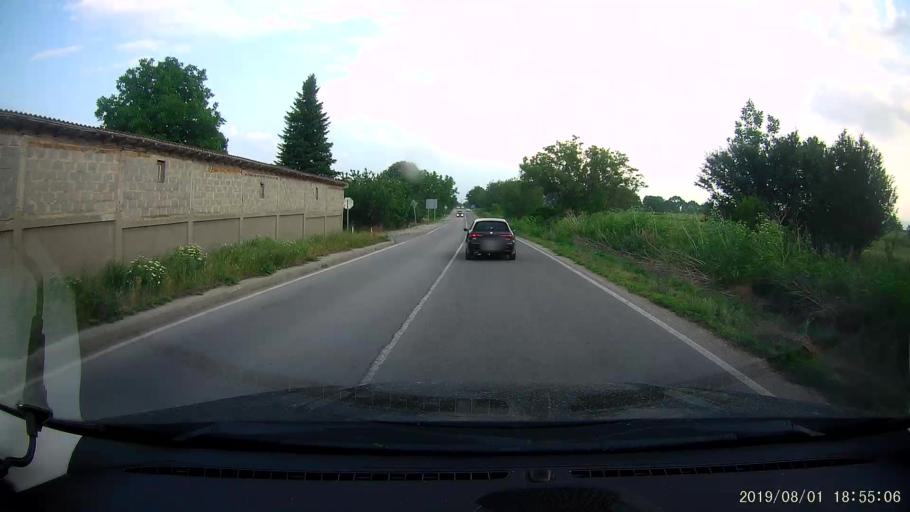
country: BG
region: Shumen
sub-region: Obshtina Shumen
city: Shumen
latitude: 43.1857
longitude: 27.0041
